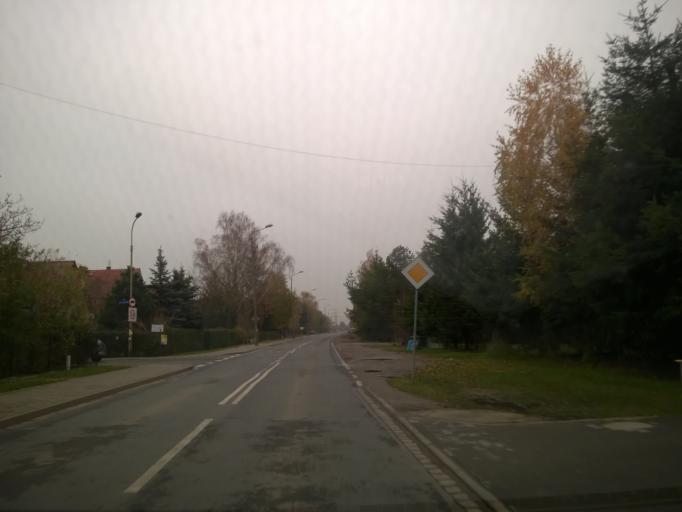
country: PL
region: Lower Silesian Voivodeship
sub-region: Powiat wroclawski
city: Zerniki Wroclawskie
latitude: 51.0613
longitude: 17.0325
